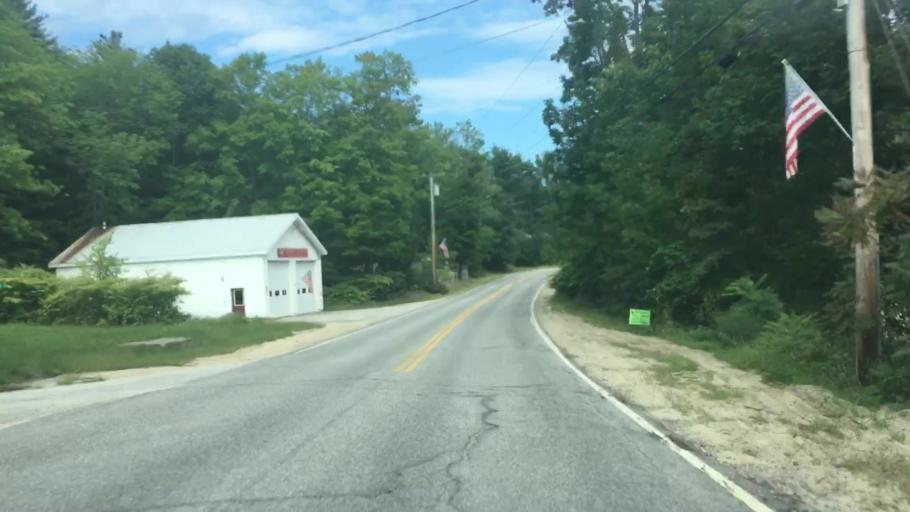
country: US
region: Maine
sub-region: Oxford County
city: Oxford
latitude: 44.0947
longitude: -70.5246
